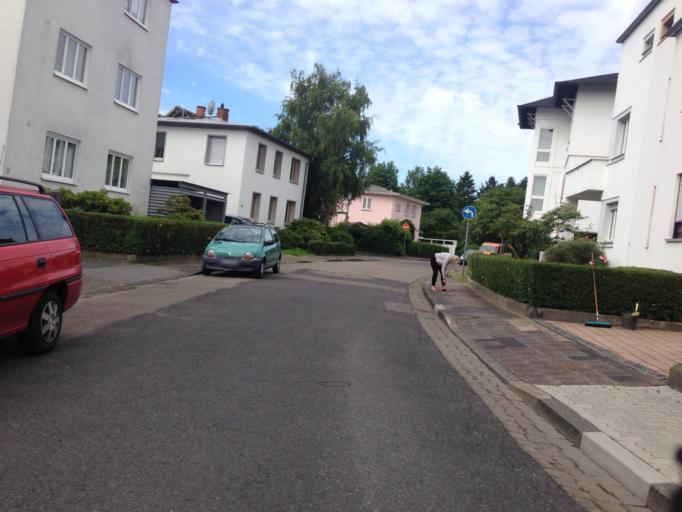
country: DE
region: Hesse
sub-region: Regierungsbezirk Darmstadt
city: Hanau am Main
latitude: 50.1423
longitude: 8.8956
